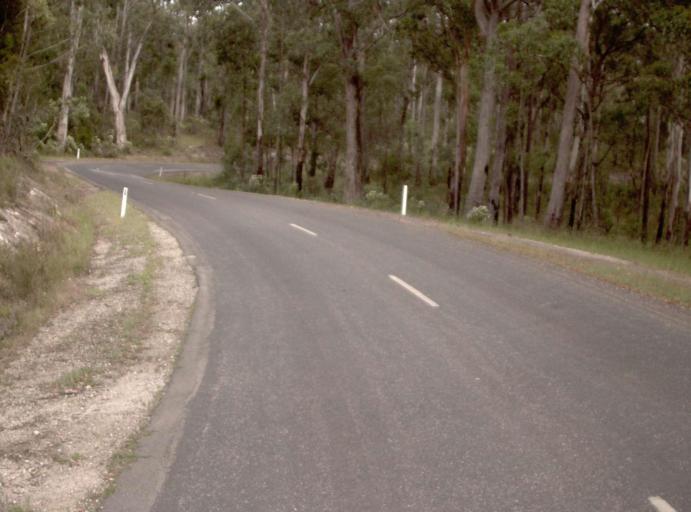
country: AU
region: Victoria
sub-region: East Gippsland
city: Bairnsdale
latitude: -37.7079
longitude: 147.5936
